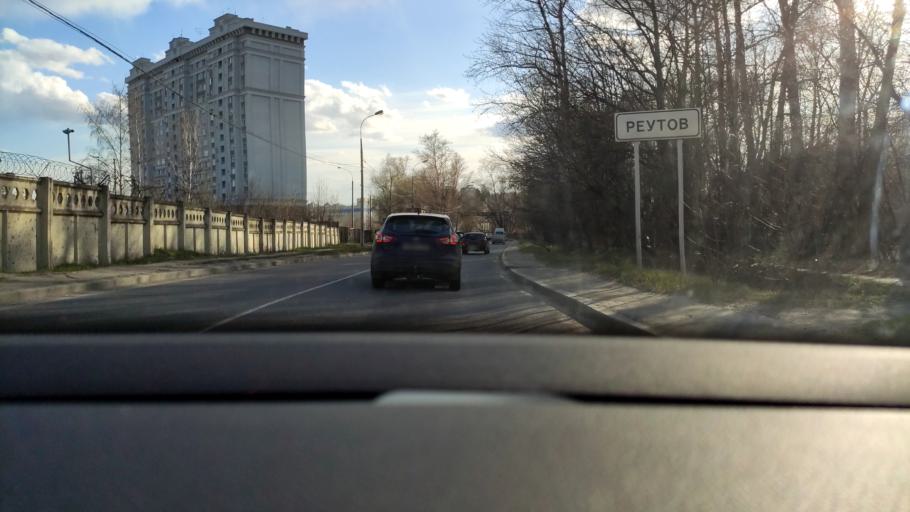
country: RU
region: Moskovskaya
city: Reutov
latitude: 55.7821
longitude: 37.8681
